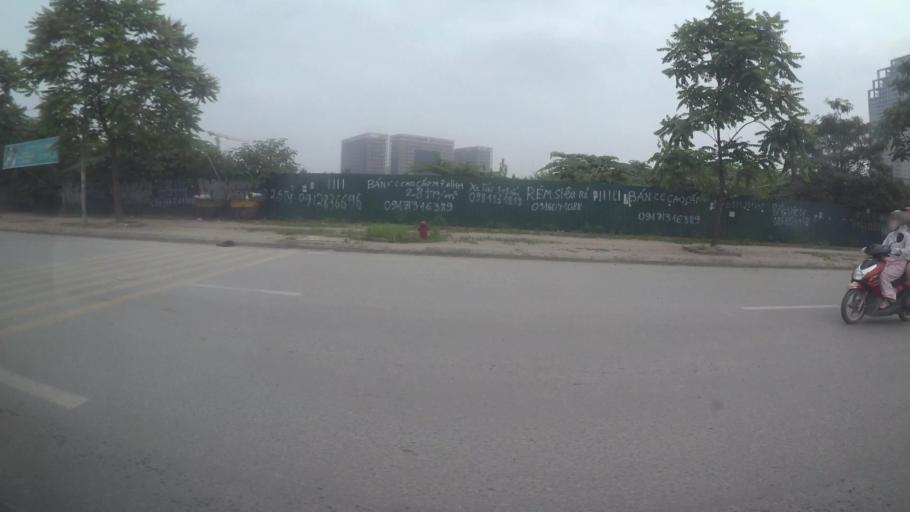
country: VN
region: Ha Noi
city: Cau Dien
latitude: 21.0100
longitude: 105.7715
